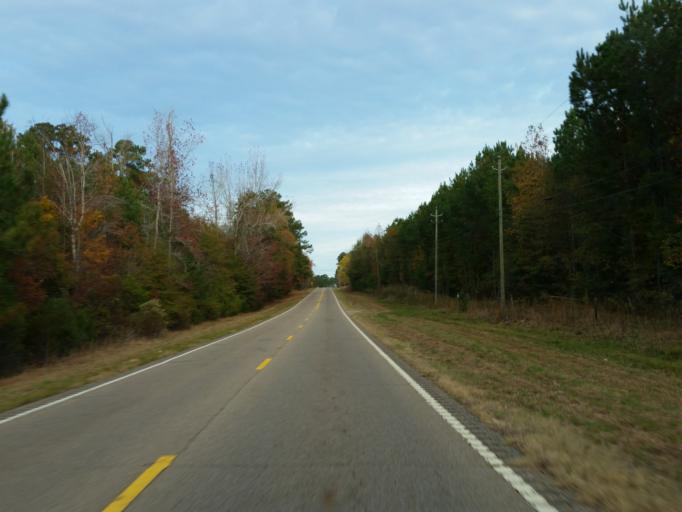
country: US
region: Mississippi
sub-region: Lauderdale County
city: Marion
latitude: 32.4076
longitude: -88.5830
